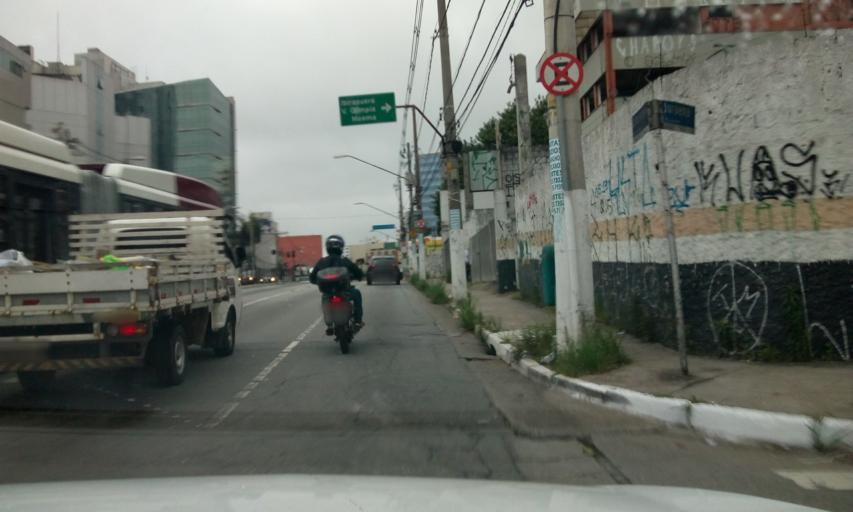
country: BR
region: Sao Paulo
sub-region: Sao Paulo
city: Sao Paulo
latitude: -23.6062
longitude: -46.6756
